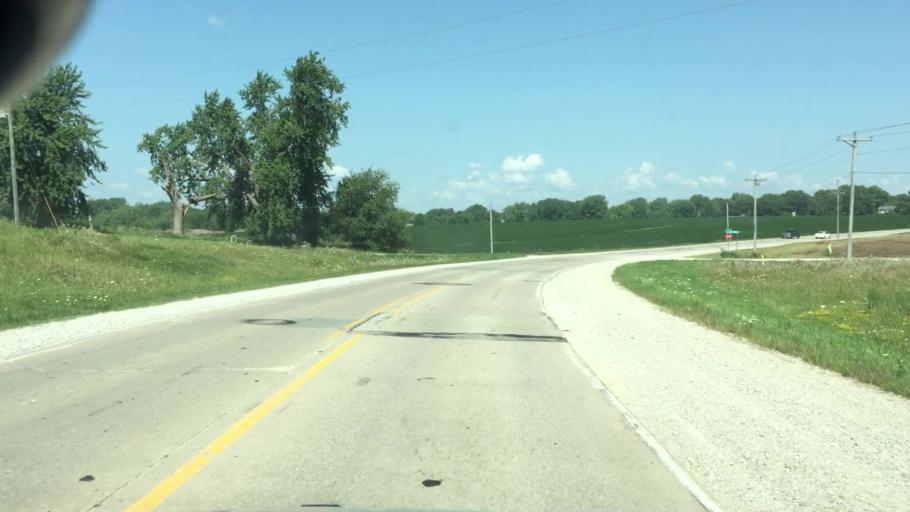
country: US
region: Iowa
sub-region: Jasper County
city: Newton
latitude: 41.6912
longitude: -93.0135
